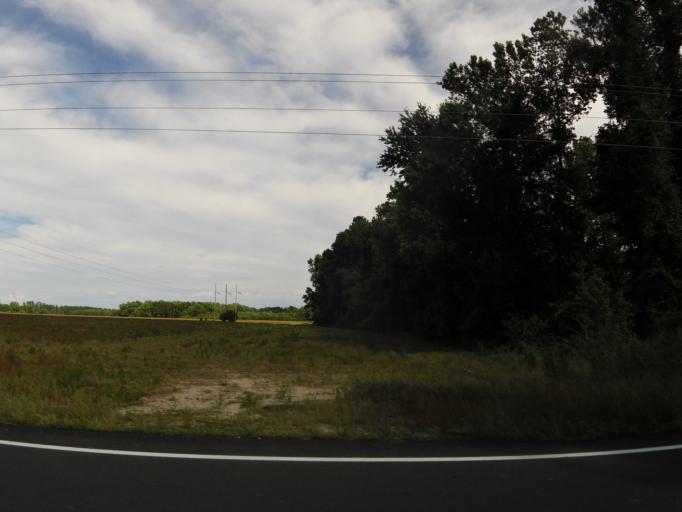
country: US
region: South Carolina
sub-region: Allendale County
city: Fairfax
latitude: 32.9797
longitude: -81.2281
